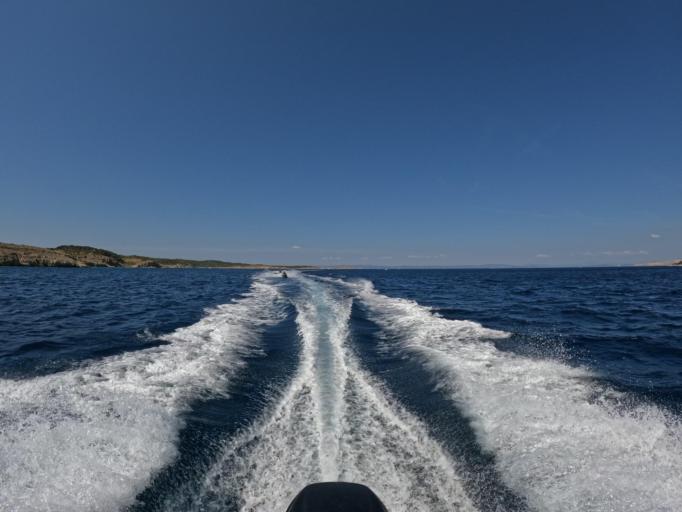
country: HR
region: Primorsko-Goranska
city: Lopar
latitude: 44.8525
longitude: 14.7513
